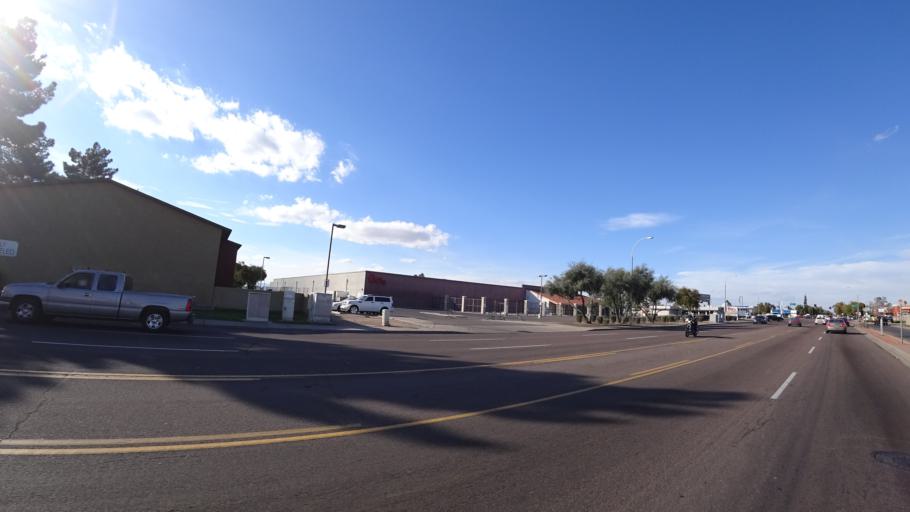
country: US
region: Arizona
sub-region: Maricopa County
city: Tolleson
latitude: 33.4920
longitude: -112.2377
